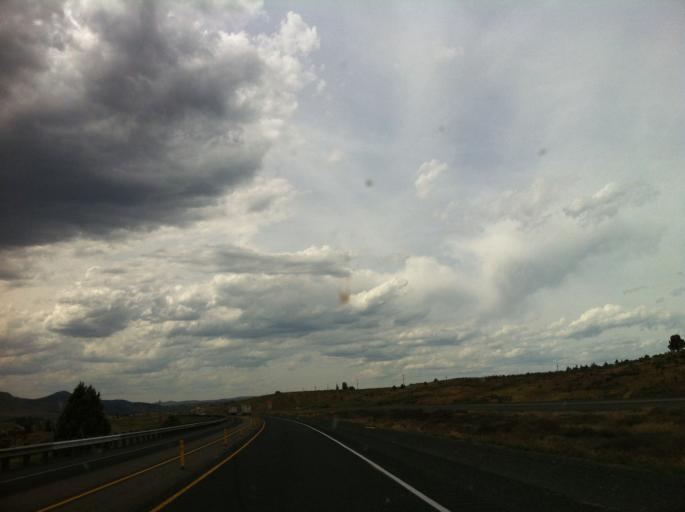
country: US
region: Oregon
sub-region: Baker County
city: Baker City
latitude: 44.5549
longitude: -117.4255
